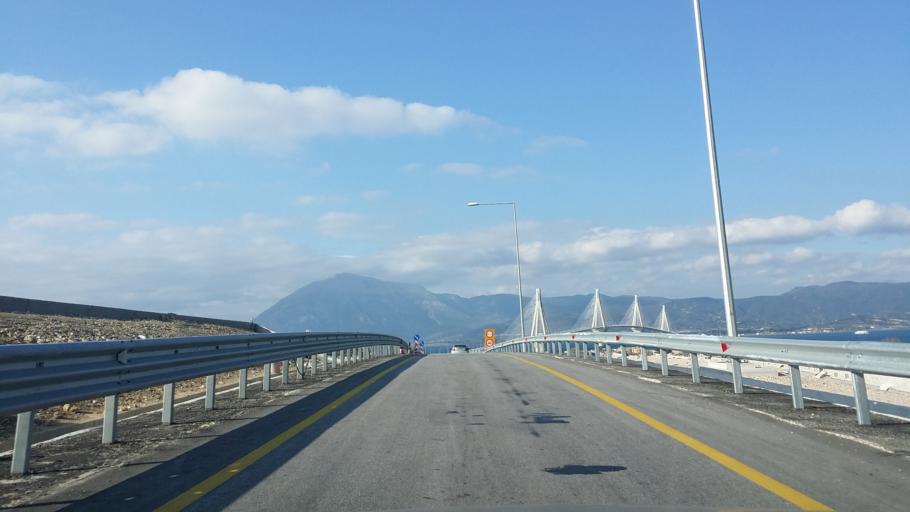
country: GR
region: West Greece
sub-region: Nomos Achaias
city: Rio
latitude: 38.3007
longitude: 21.7913
